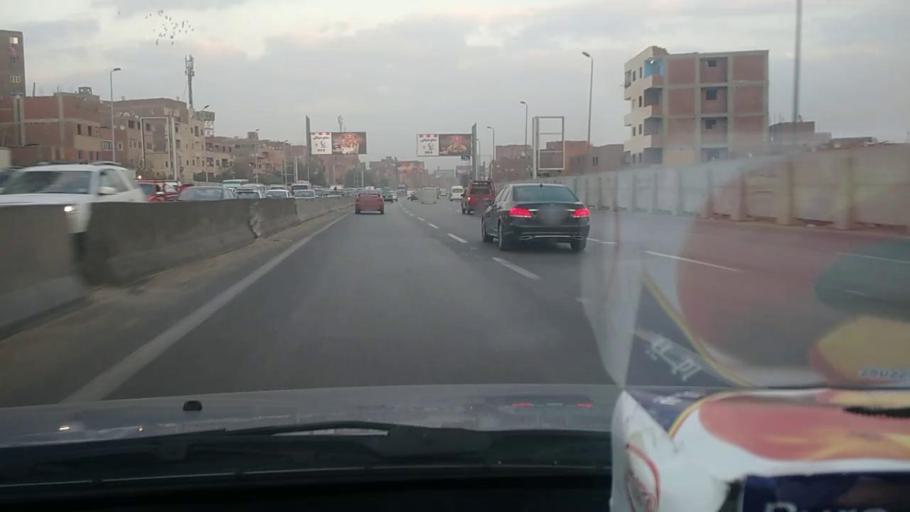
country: EG
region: Al Jizah
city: Al Jizah
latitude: 29.9927
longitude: 31.2452
